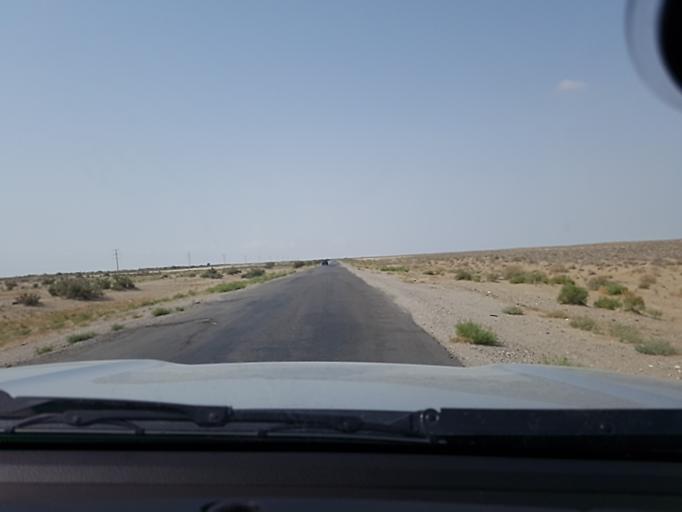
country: TM
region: Balkan
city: Gumdag
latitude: 38.7869
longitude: 54.5962
